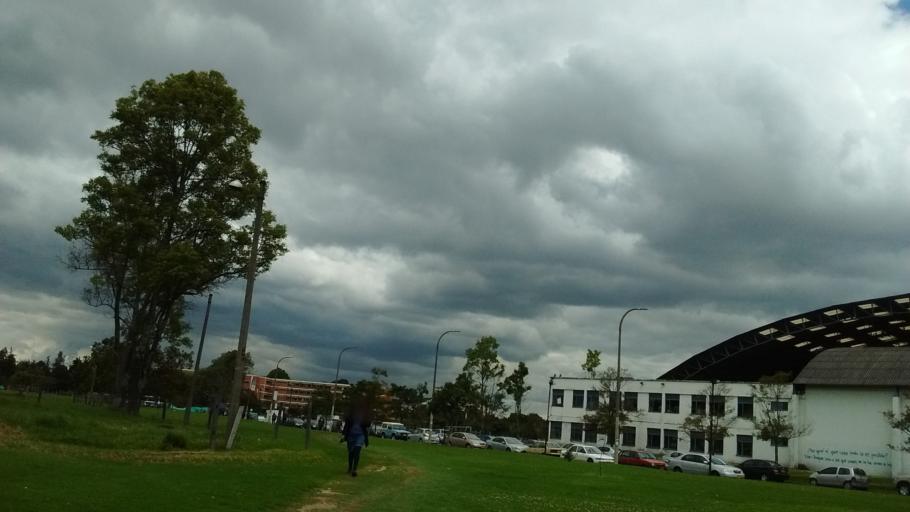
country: CO
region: Bogota D.C.
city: Bogota
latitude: 4.6379
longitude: -74.0870
